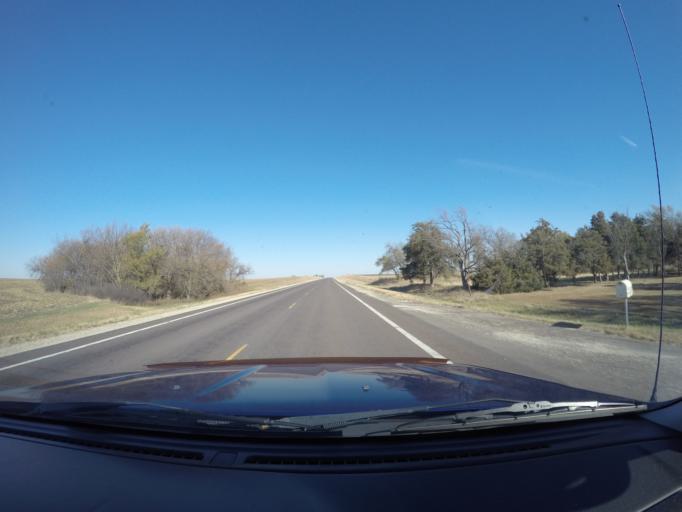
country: US
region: Kansas
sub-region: Marshall County
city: Blue Rapids
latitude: 39.6256
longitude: -96.7504
